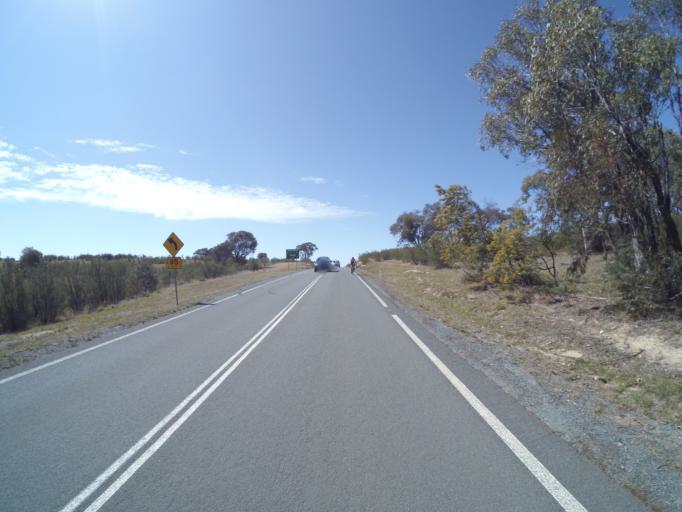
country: AU
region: Australian Capital Territory
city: Macarthur
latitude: -35.4515
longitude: 148.9692
